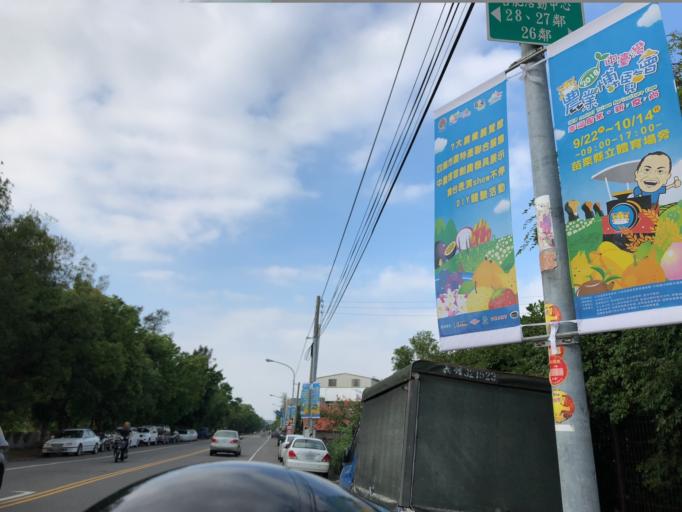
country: TW
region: Taiwan
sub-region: Miaoli
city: Miaoli
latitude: 24.5874
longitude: 120.8251
